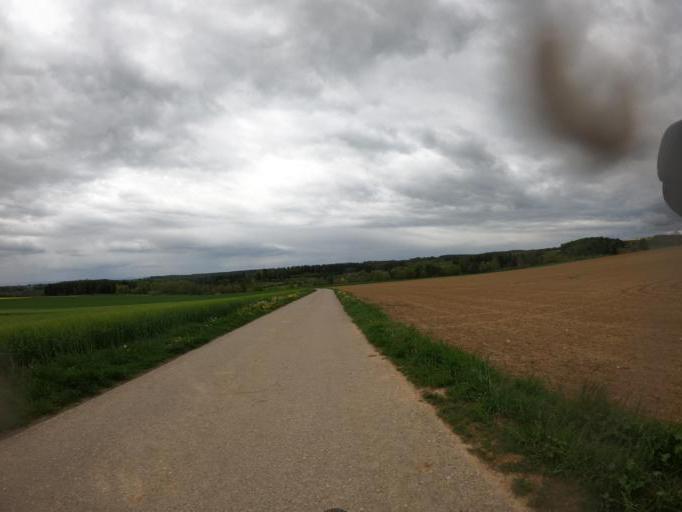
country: DE
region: Baden-Wuerttemberg
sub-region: Karlsruhe Region
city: Nagold
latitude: 48.5253
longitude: 8.6961
